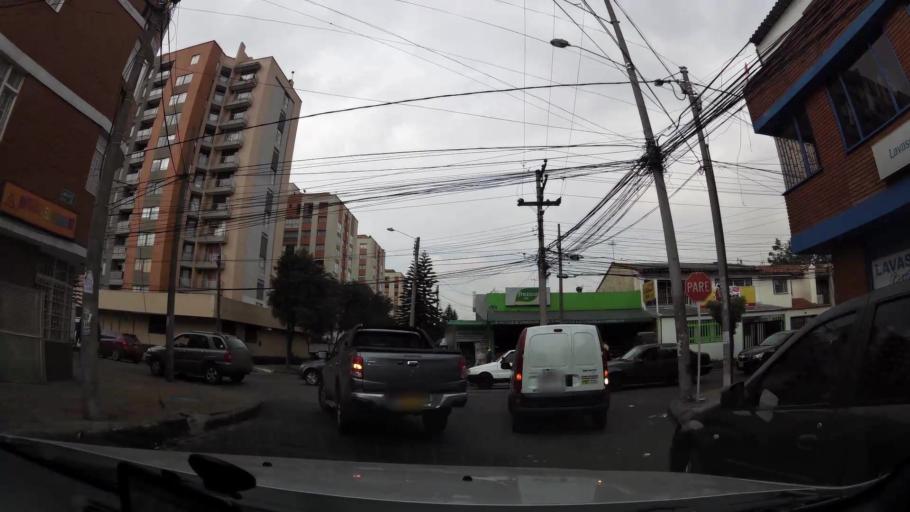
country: CO
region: Bogota D.C.
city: Barrio San Luis
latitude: 4.6893
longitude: -74.0747
